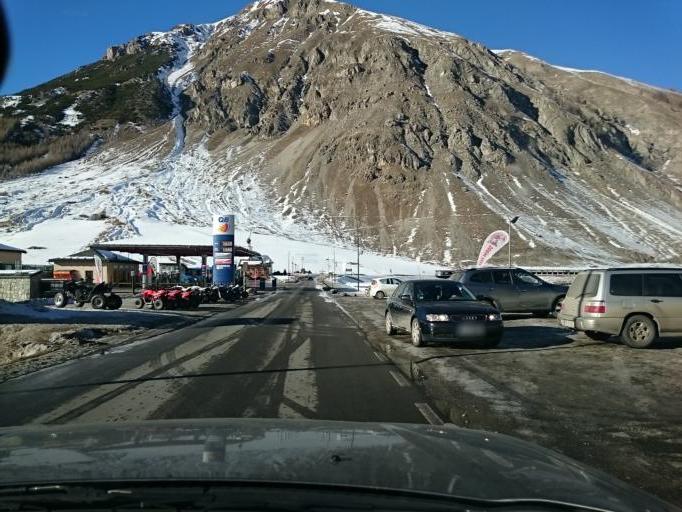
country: IT
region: Lombardy
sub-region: Provincia di Sondrio
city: Livigno
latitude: 46.5561
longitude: 10.1445
